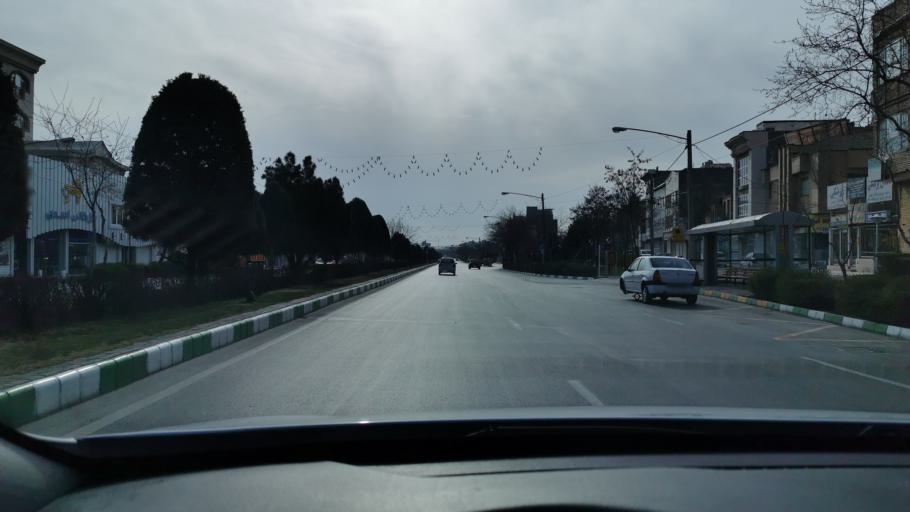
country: IR
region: Razavi Khorasan
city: Mashhad
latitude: 36.3036
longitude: 59.5149
